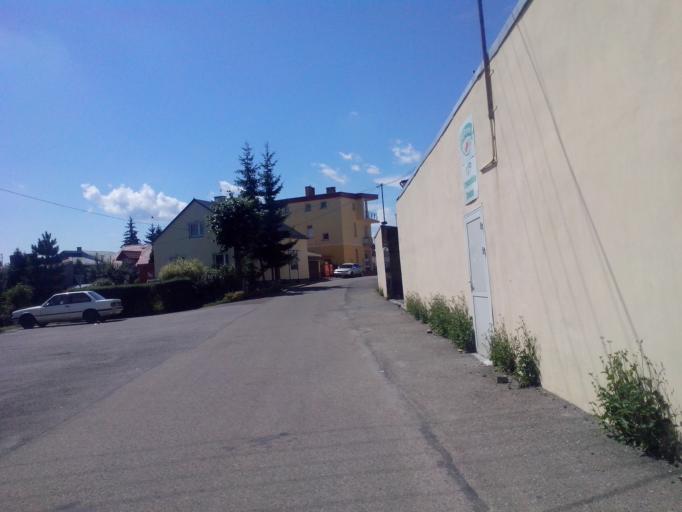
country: PL
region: Subcarpathian Voivodeship
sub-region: Powiat strzyzowski
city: Czudec
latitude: 49.9465
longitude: 21.8396
